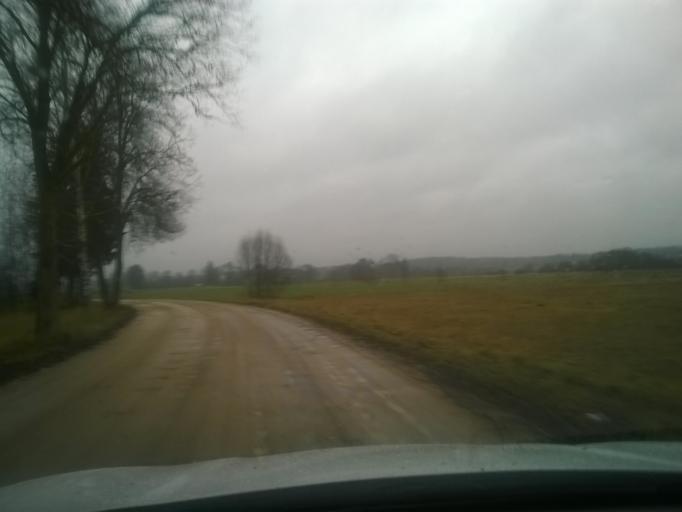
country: LV
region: Jaunpils
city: Jaunpils
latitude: 56.9105
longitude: 22.9687
